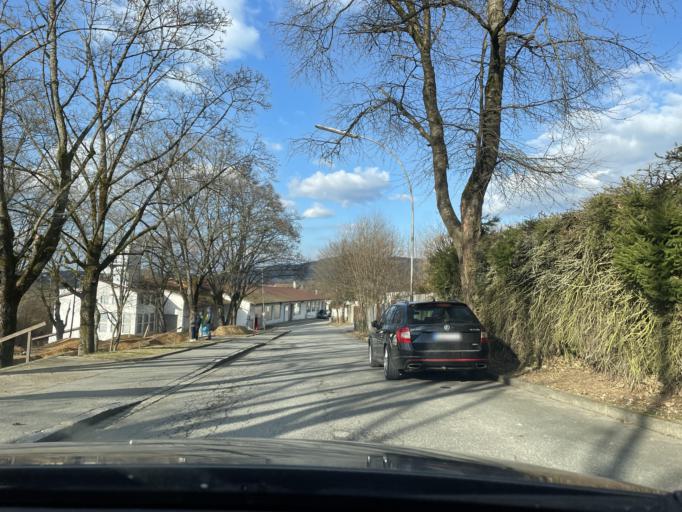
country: DE
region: Bavaria
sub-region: Lower Bavaria
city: Viechtach
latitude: 49.0756
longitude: 12.8838
